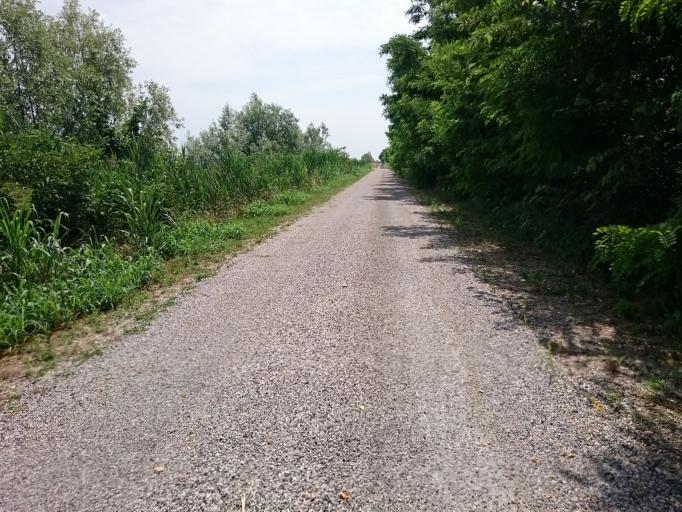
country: IT
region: Veneto
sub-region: Provincia di Venezia
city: Valli
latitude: 45.2142
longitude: 12.1644
